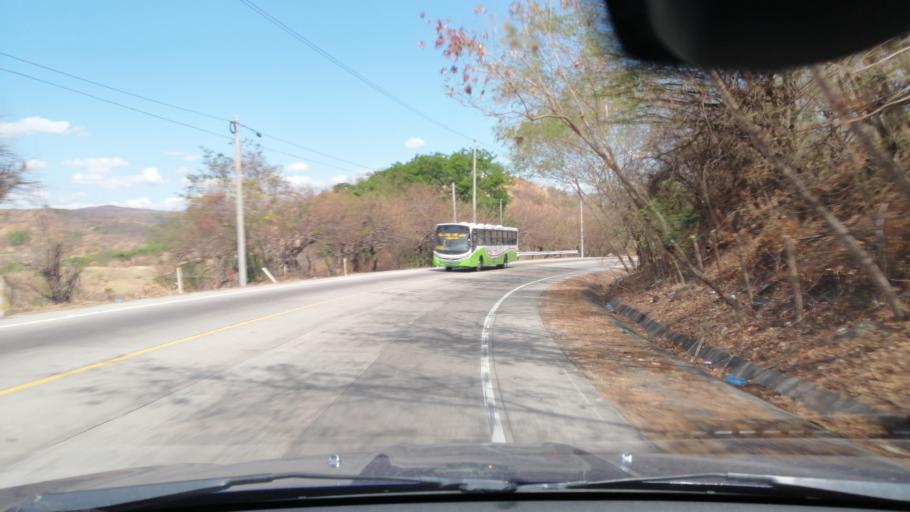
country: SV
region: Santa Ana
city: Texistepeque
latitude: 14.1894
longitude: -89.4968
